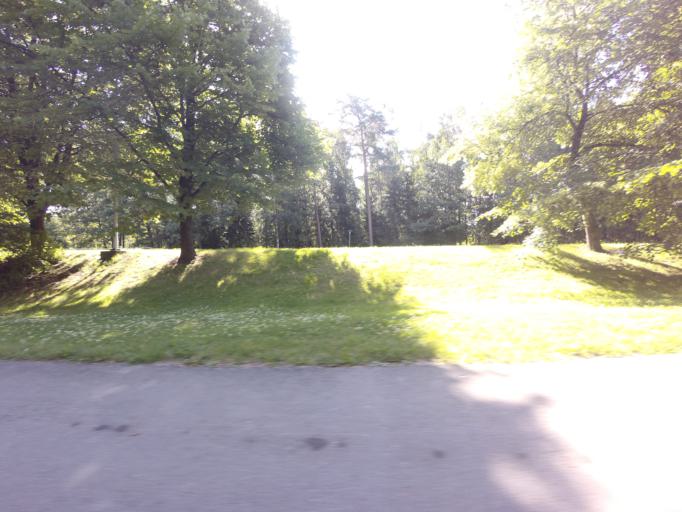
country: FI
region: Uusimaa
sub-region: Helsinki
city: Espoo
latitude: 60.1495
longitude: 24.6440
